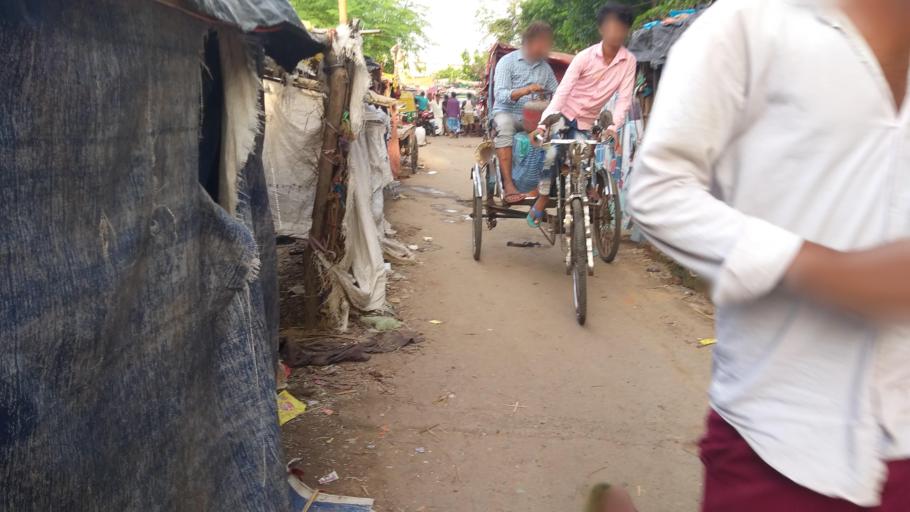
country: IN
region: Bihar
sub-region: Patna
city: Patna
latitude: 25.6044
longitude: 85.1296
